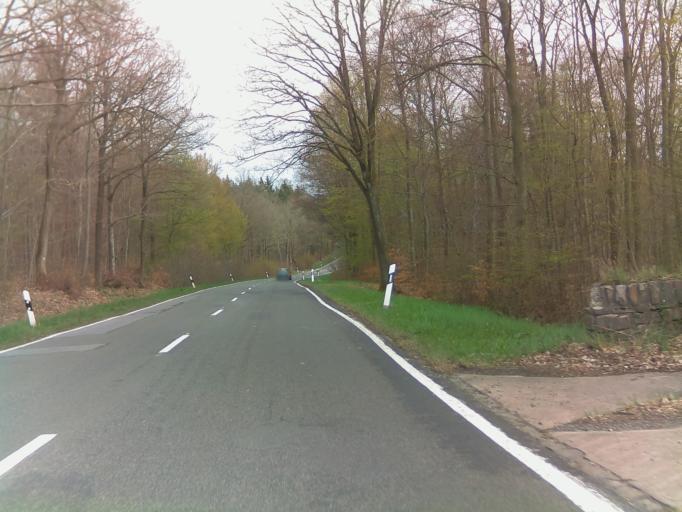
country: DE
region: Rheinland-Pfalz
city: Seesbach
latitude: 49.8733
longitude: 7.5525
